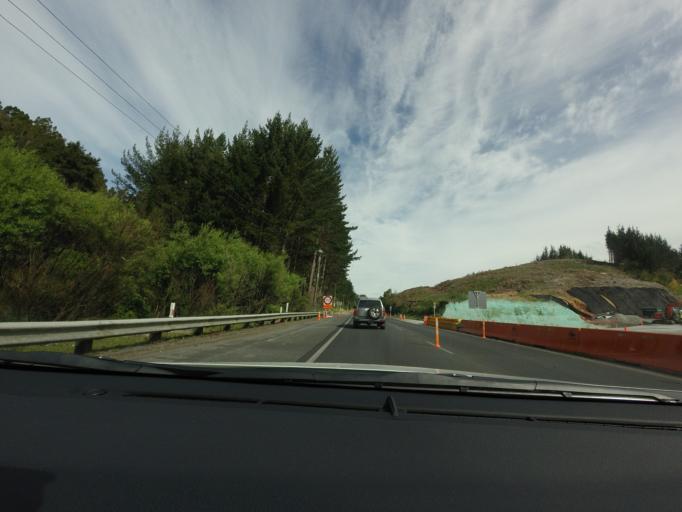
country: NZ
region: Auckland
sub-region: Auckland
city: Warkworth
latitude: -36.4947
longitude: 174.6597
